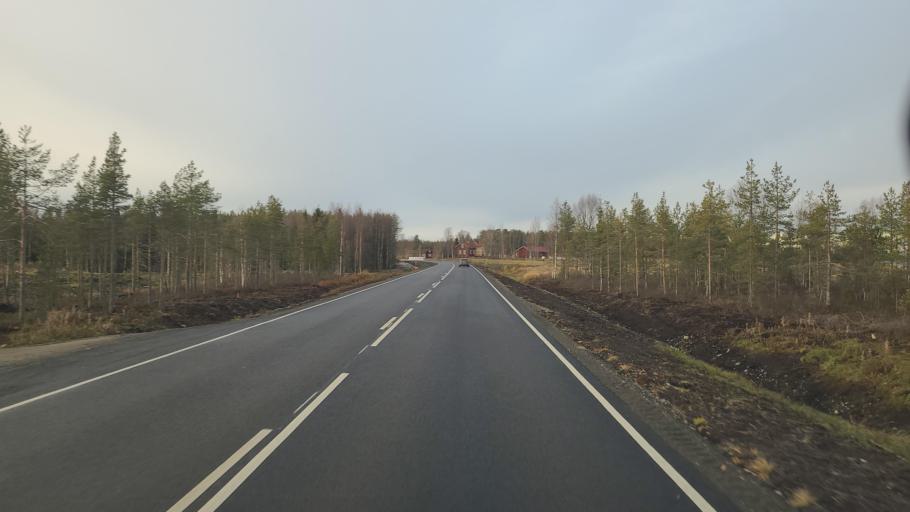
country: FI
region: Lapland
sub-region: Tunturi-Lappi
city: Kittilae
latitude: 67.8761
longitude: 24.8878
